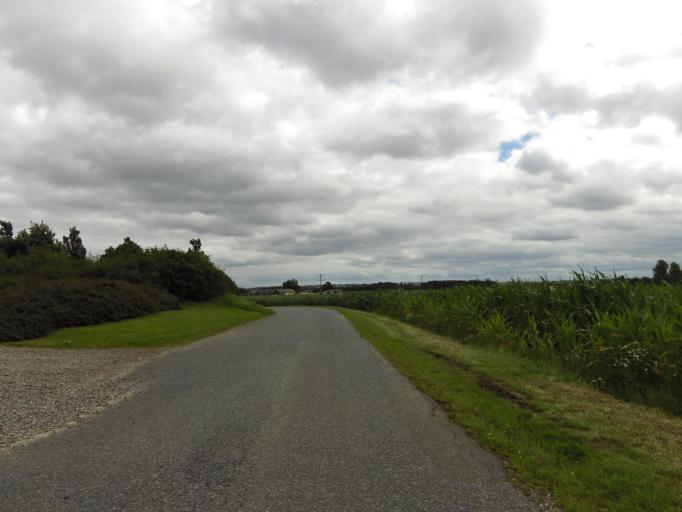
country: DK
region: South Denmark
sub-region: Haderslev Kommune
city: Gram
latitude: 55.3028
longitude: 9.1457
